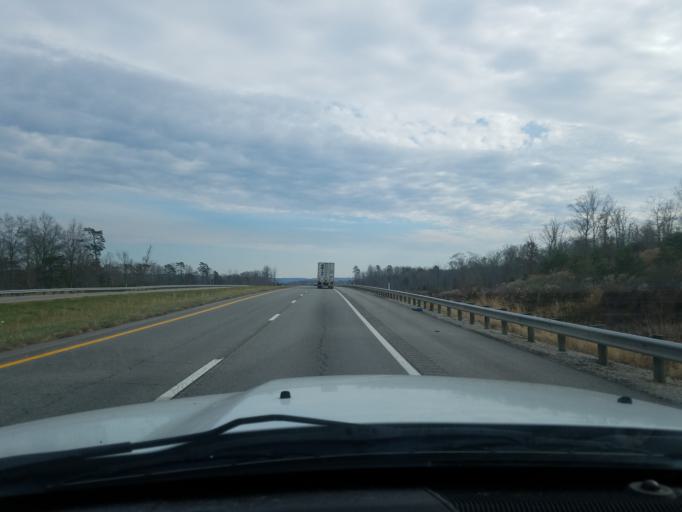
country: US
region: West Virginia
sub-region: Putnam County
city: Eleanor
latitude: 38.5534
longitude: -81.9945
